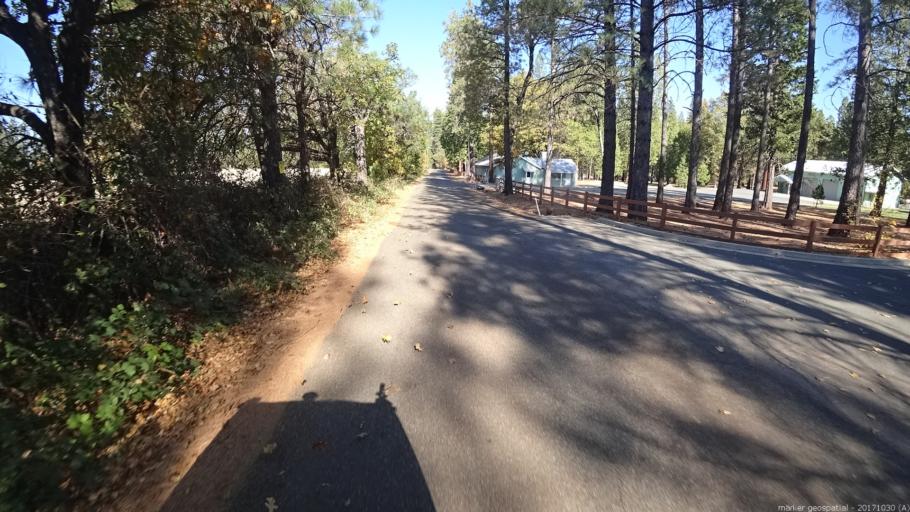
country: US
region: California
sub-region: Shasta County
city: Shingletown
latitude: 40.6307
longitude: -121.8950
